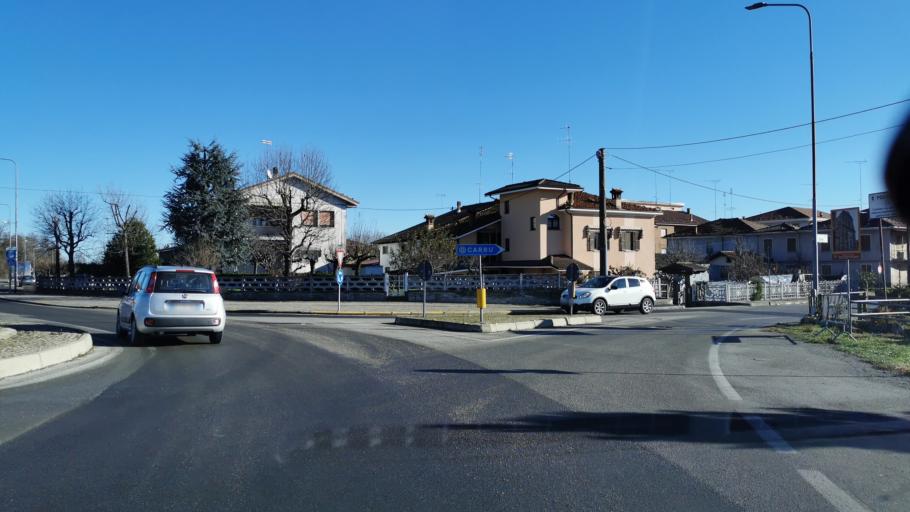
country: IT
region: Piedmont
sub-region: Provincia di Cuneo
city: Carru
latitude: 44.4796
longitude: 7.8683
